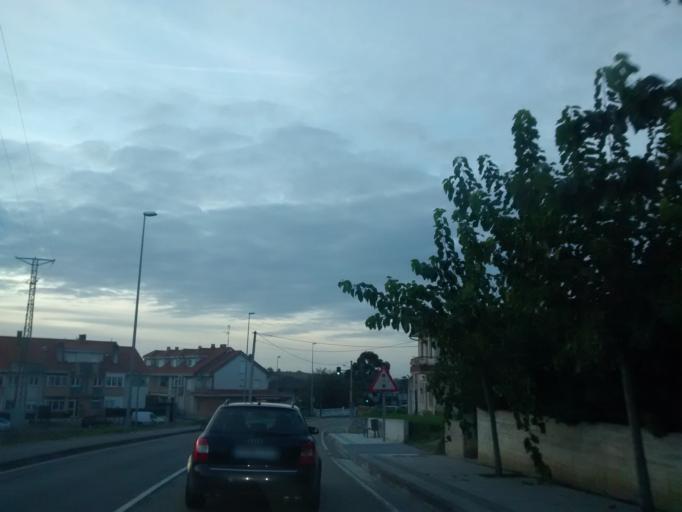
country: ES
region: Cantabria
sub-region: Provincia de Cantabria
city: Santa Cruz de Bezana
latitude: 43.4284
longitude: -3.9421
